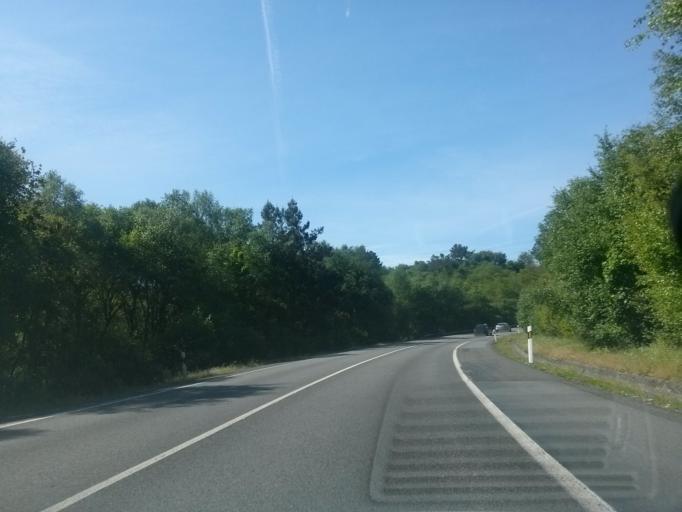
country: ES
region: Galicia
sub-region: Provincia de Lugo
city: Lugo
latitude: 43.0006
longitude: -7.5829
